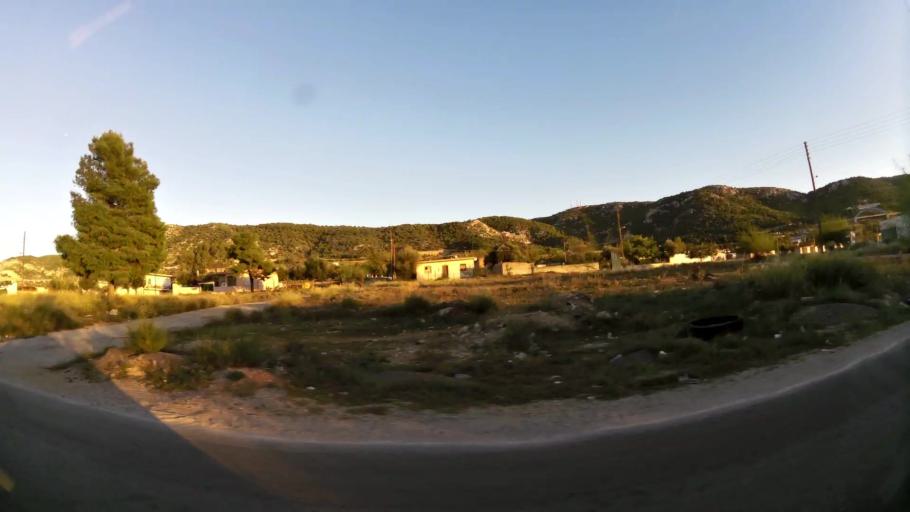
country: GR
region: Attica
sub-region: Nomarchia Athinas
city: Skaramangas
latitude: 38.0412
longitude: 23.6312
